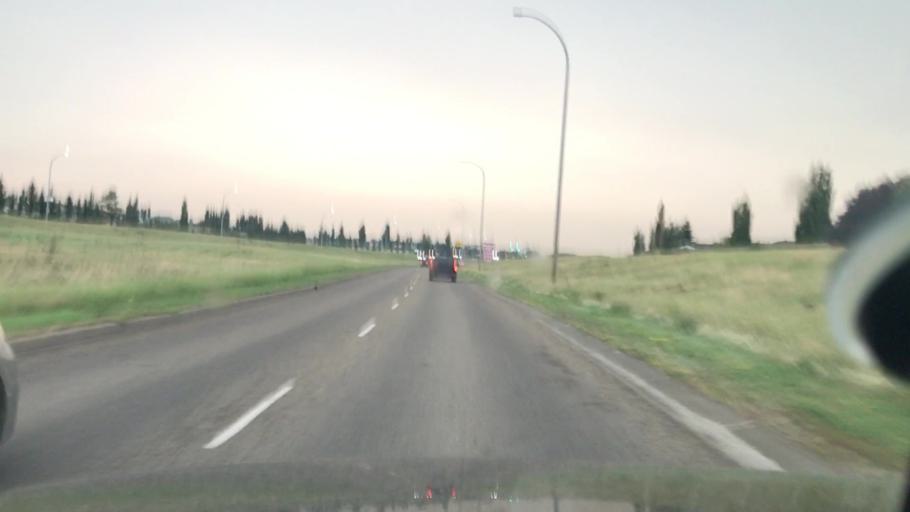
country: CA
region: Alberta
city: Edmonton
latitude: 53.4552
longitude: -113.5911
